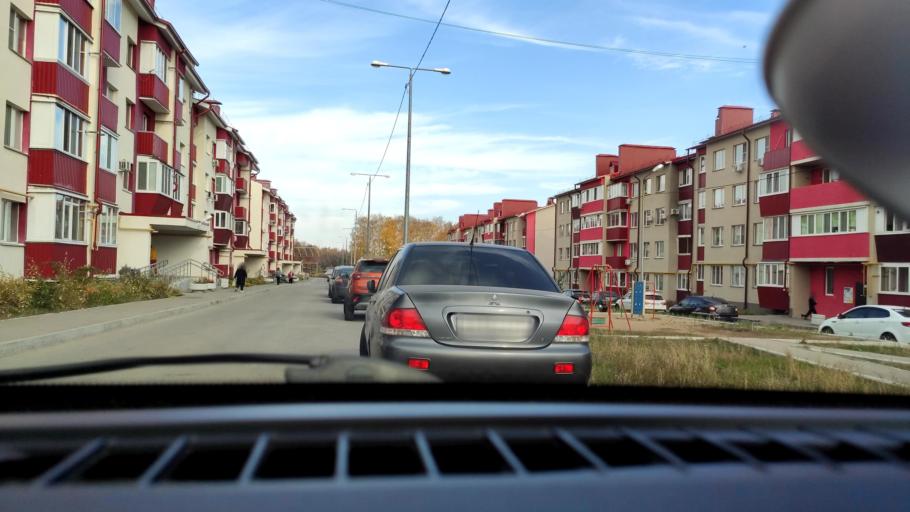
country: RU
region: Samara
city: Novosemeykino
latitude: 53.3318
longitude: 50.3146
